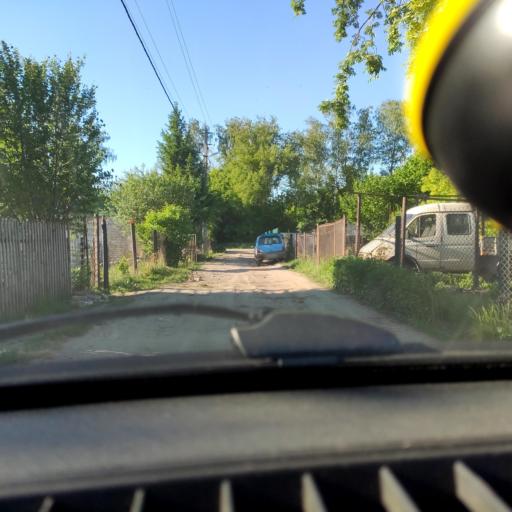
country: RU
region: Samara
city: Tol'yatti
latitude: 53.5974
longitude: 49.3154
